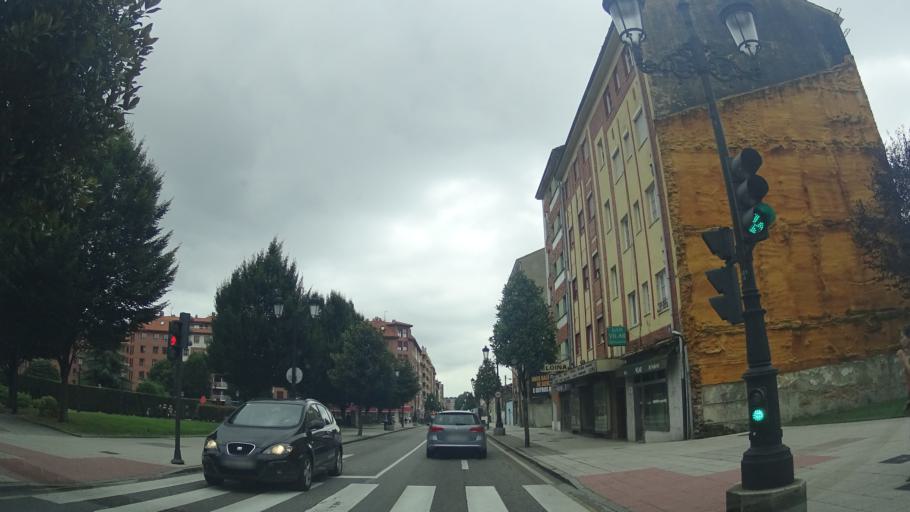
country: ES
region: Asturias
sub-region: Province of Asturias
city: Oviedo
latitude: 43.3660
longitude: -5.8309
